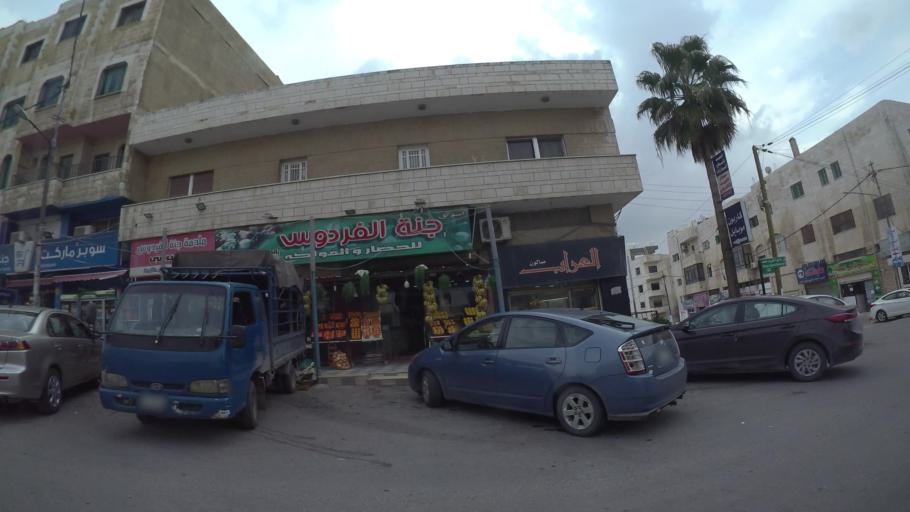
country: JO
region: Amman
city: Umm as Summaq
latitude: 31.8876
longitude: 35.8543
